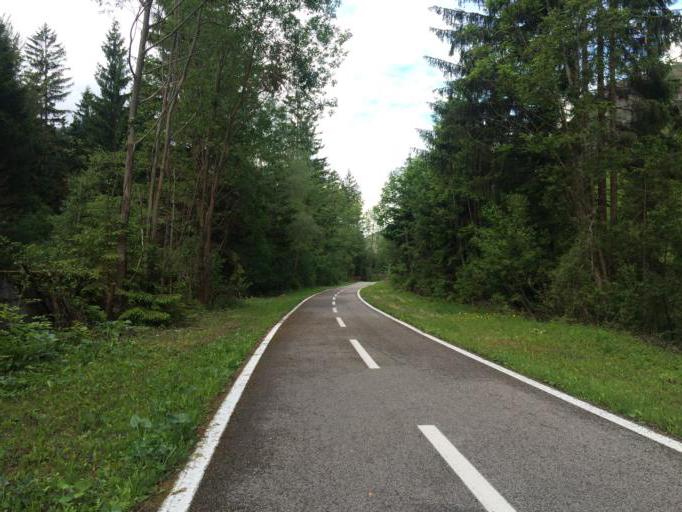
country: IT
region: Friuli Venezia Giulia
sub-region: Provincia di Udine
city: Tarvisio
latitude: 46.5030
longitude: 13.5132
